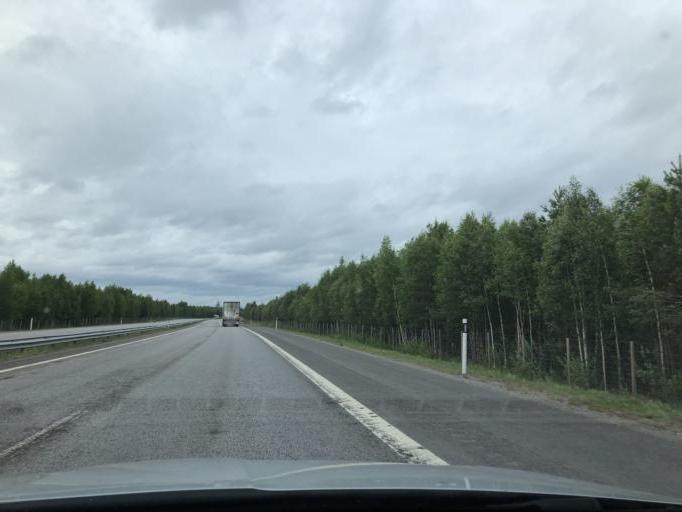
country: SE
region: Norrbotten
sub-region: Pitea Kommun
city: Pitea
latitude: 65.3554
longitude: 21.4360
